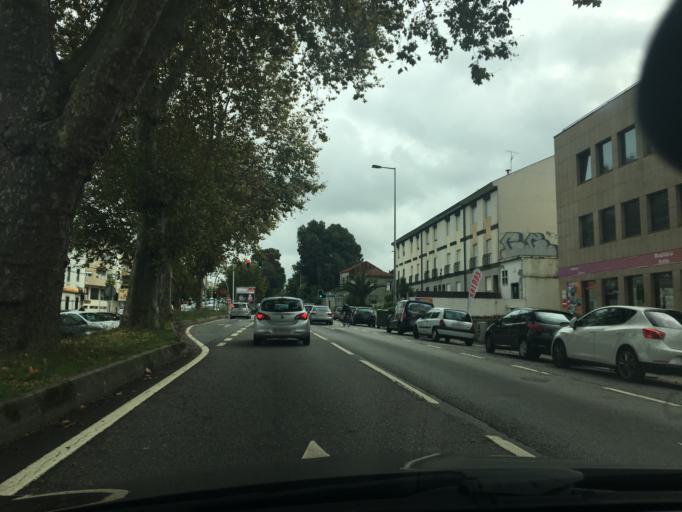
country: PT
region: Porto
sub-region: Matosinhos
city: Senhora da Hora
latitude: 41.1793
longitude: -8.6306
